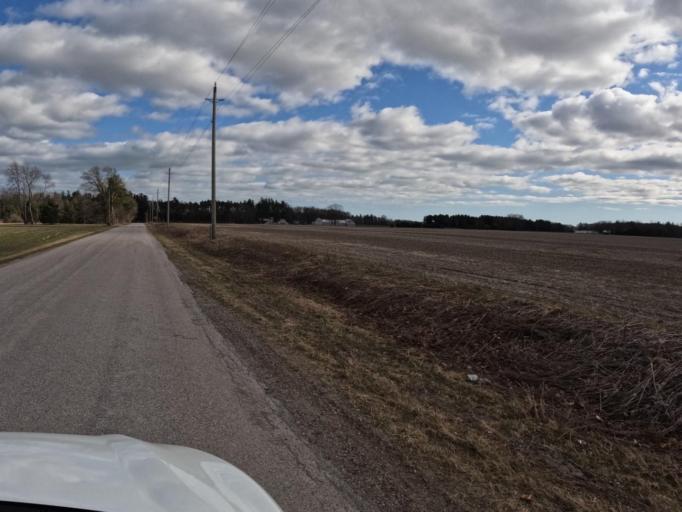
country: CA
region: Ontario
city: Norfolk County
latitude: 42.7435
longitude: -80.3807
